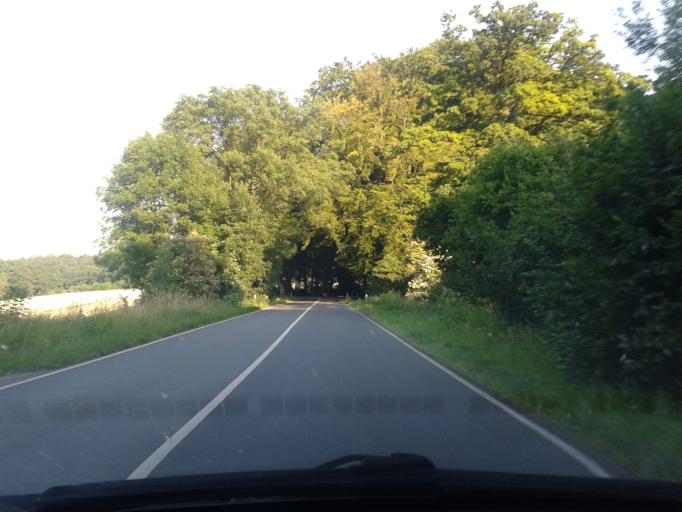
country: DE
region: North Rhine-Westphalia
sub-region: Regierungsbezirk Detmold
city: Lemgo
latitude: 52.0002
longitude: 8.9165
